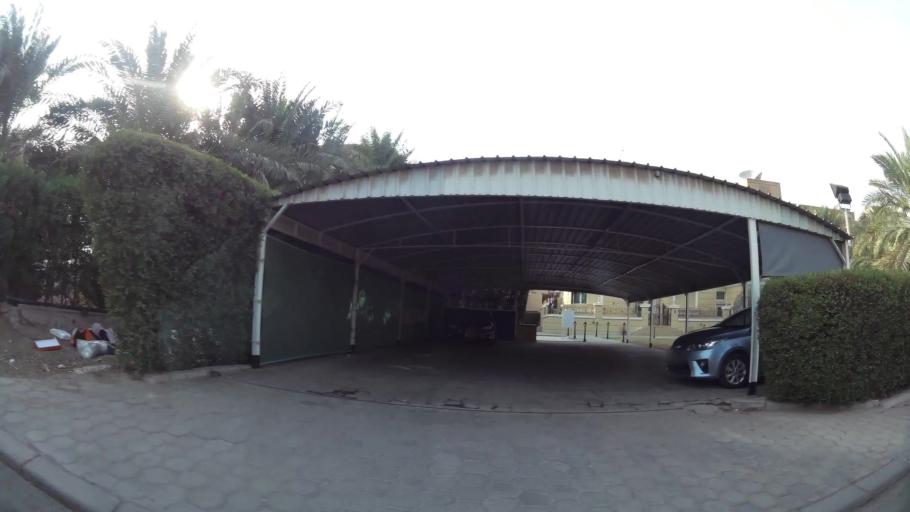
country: KW
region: Mubarak al Kabir
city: Sabah as Salim
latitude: 29.2266
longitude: 48.0600
